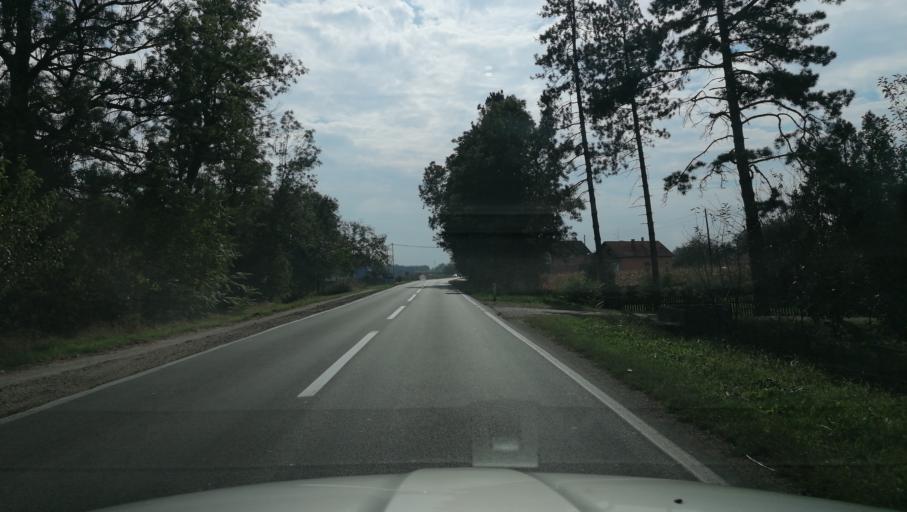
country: BA
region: Republika Srpska
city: Dvorovi
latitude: 44.8394
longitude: 19.2969
